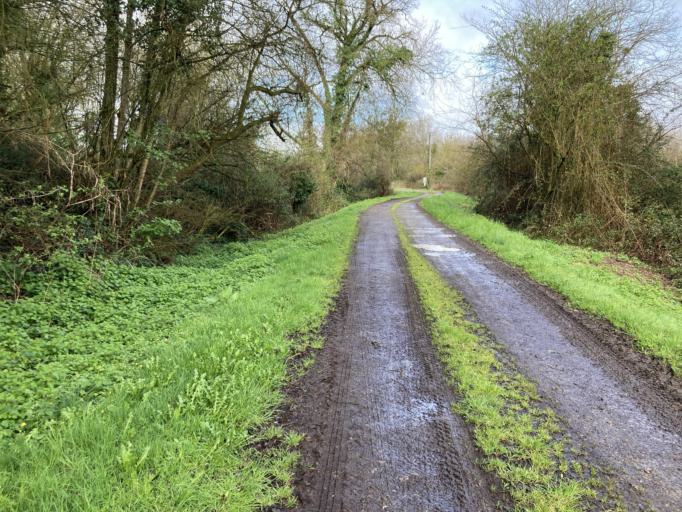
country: FR
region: Aquitaine
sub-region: Departement des Landes
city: Souprosse
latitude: 43.7619
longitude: -0.6689
